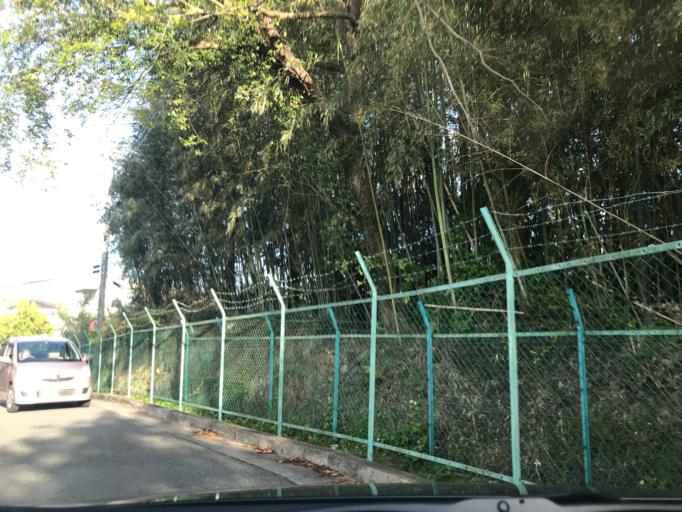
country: JP
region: Hyogo
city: Kawanishi
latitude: 34.8623
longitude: 135.4031
